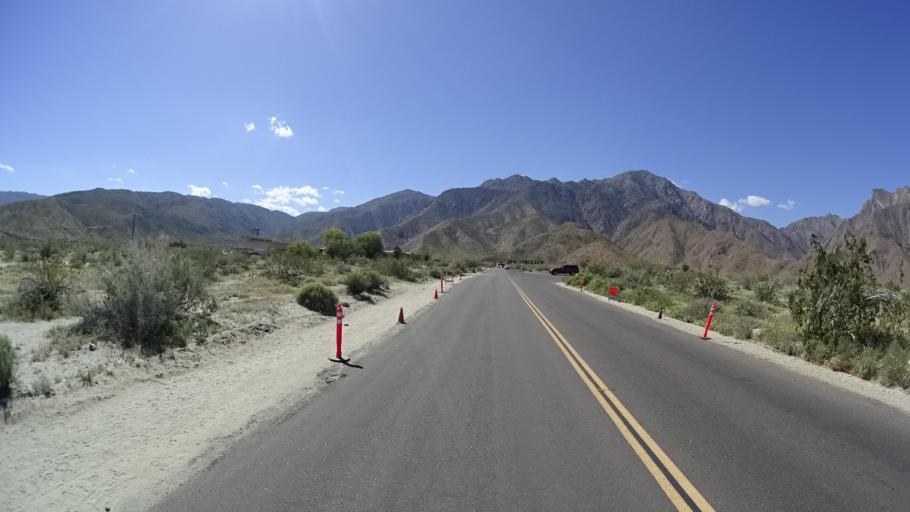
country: US
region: California
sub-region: San Diego County
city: Borrego Springs
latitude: 33.2568
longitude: -116.4013
